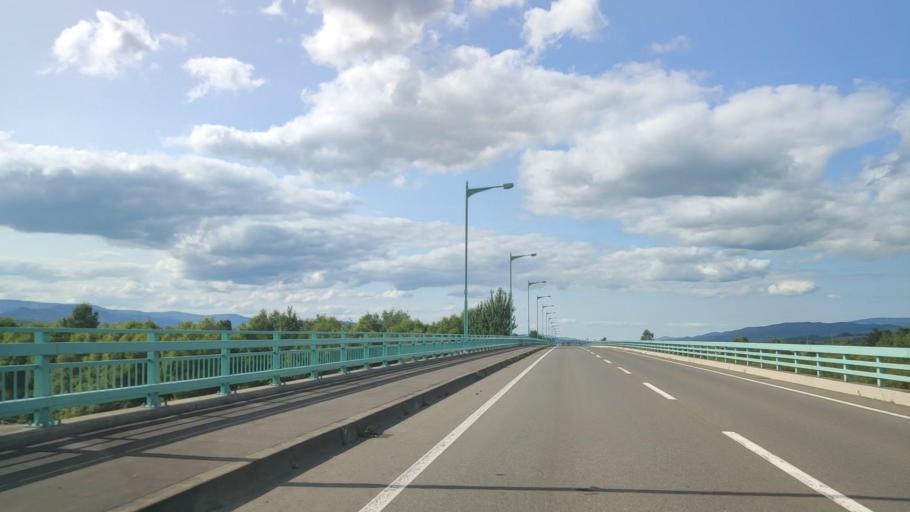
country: JP
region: Hokkaido
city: Nayoro
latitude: 44.4544
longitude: 142.3595
